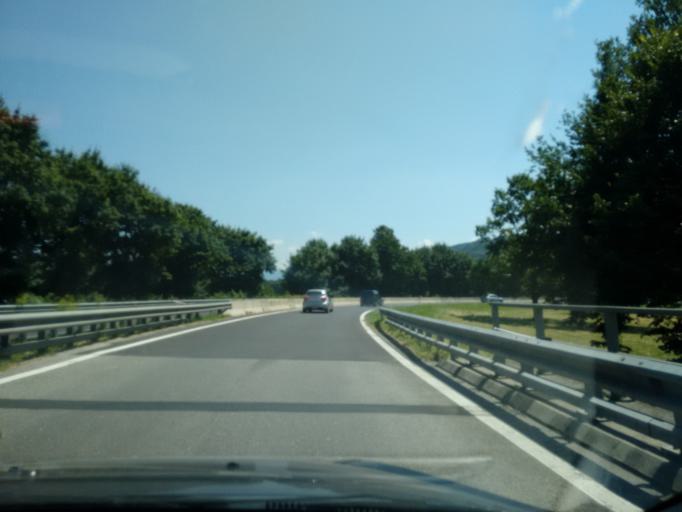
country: AT
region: Upper Austria
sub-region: Politischer Bezirk Vocklabruck
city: Attnang-Puchheim
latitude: 47.9558
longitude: 13.7332
